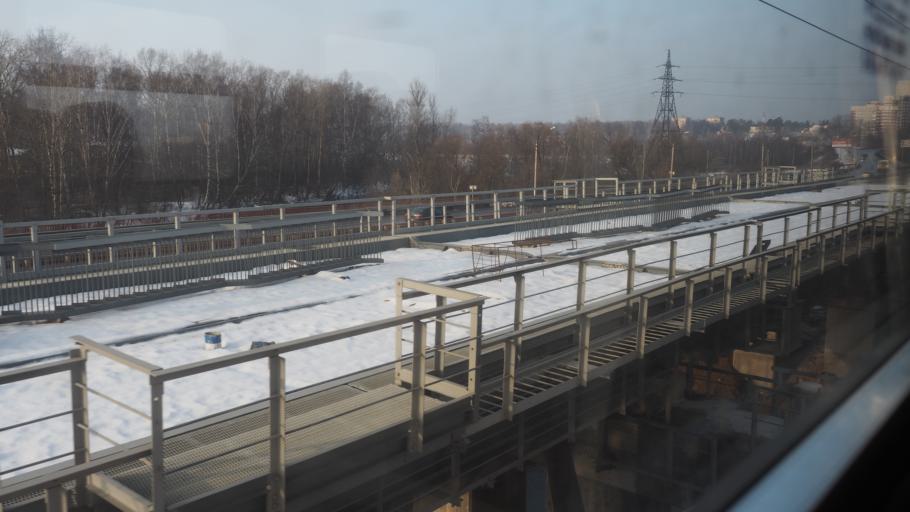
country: RU
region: Moskovskaya
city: Mamontovka
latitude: 55.9967
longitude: 37.8304
